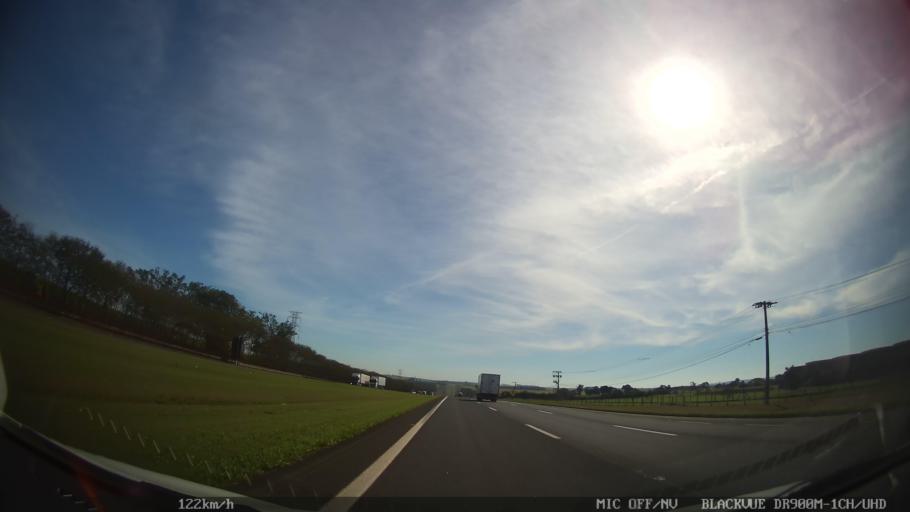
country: BR
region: Sao Paulo
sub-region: Araras
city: Araras
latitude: -22.3219
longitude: -47.3899
